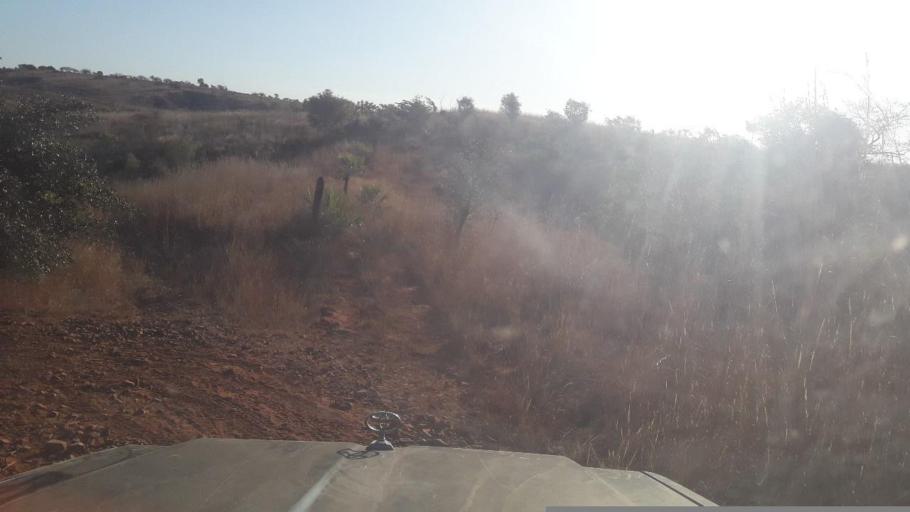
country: MG
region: Boeny
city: Sitampiky
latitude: -16.4924
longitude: 45.6071
